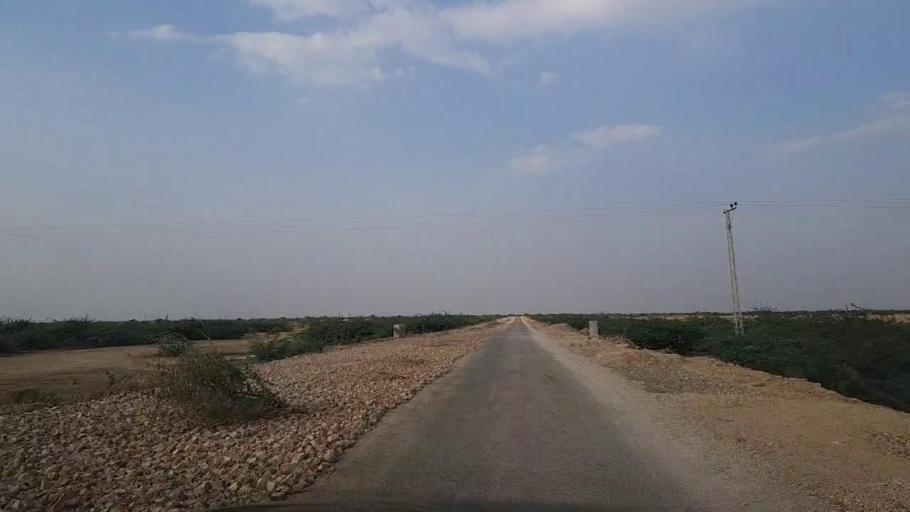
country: PK
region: Sindh
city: Gharo
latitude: 24.8411
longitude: 67.7461
